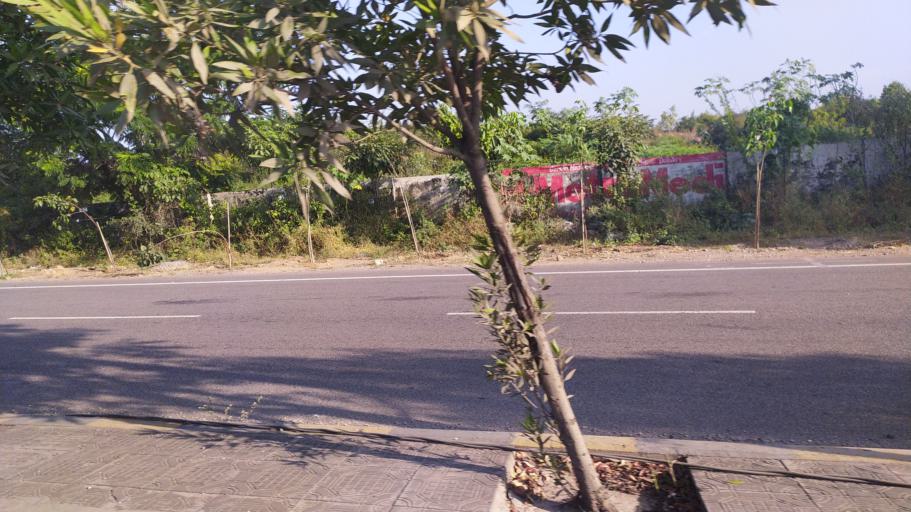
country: IN
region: Telangana
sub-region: Hyderabad
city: Hyderabad
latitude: 17.3202
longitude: 78.3882
